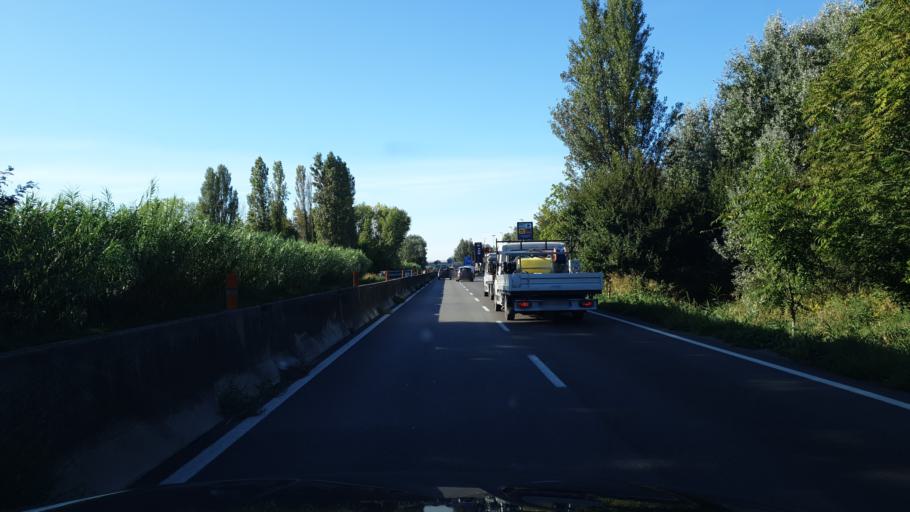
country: IT
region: Emilia-Romagna
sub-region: Provincia di Ravenna
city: Ravenna
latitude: 44.4057
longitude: 12.1763
